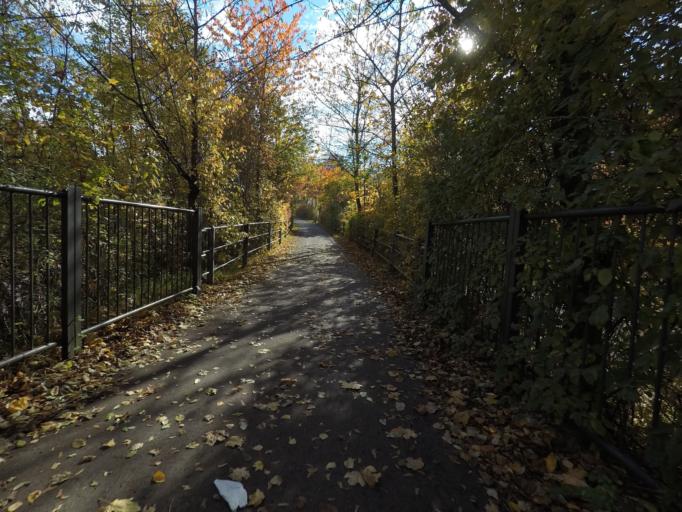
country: DE
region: Baden-Wuerttemberg
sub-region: Tuebingen Region
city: Pfullingen
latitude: 48.4543
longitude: 9.2308
